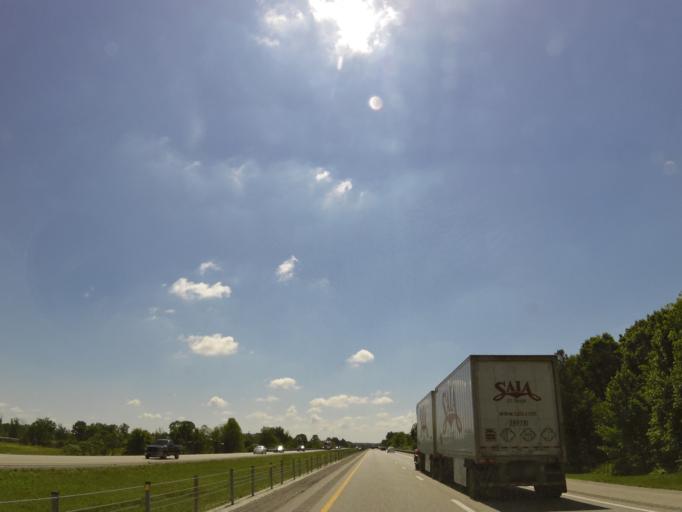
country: US
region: Kentucky
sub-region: Laurel County
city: London
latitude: 37.2092
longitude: -84.1762
